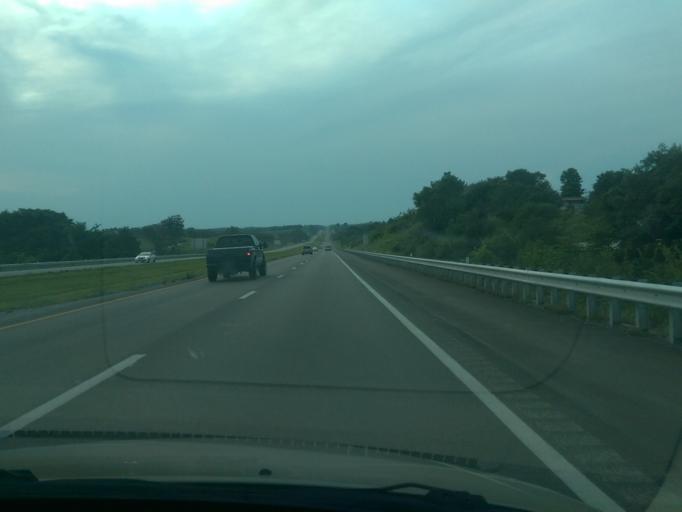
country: US
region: Missouri
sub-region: Andrew County
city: Country Club Village
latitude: 39.8627
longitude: -94.8178
